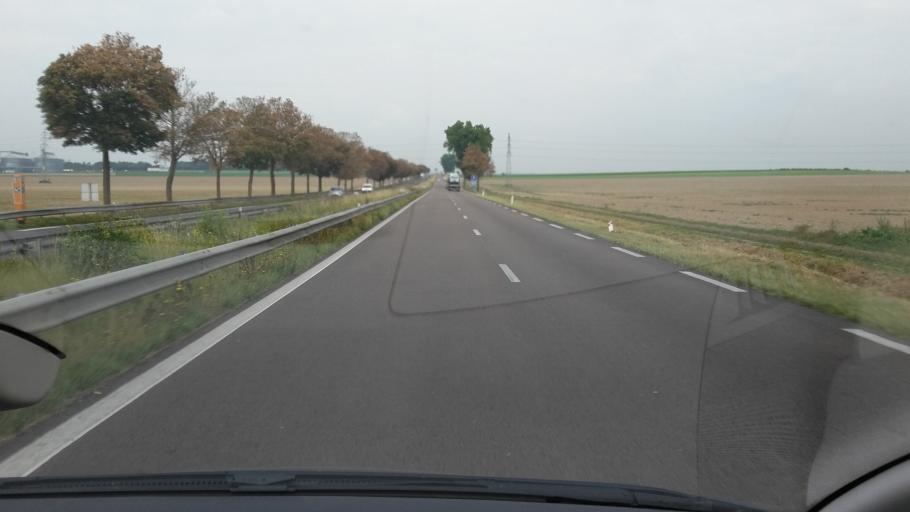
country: FR
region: Champagne-Ardenne
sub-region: Departement de la Marne
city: Bazancourt
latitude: 49.3282
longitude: 4.1671
